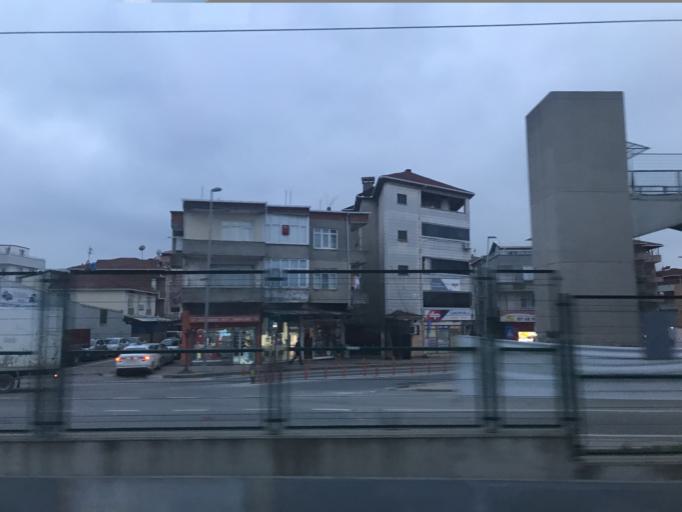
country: TR
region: Kocaeli
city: Darica
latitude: 40.7858
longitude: 29.4042
